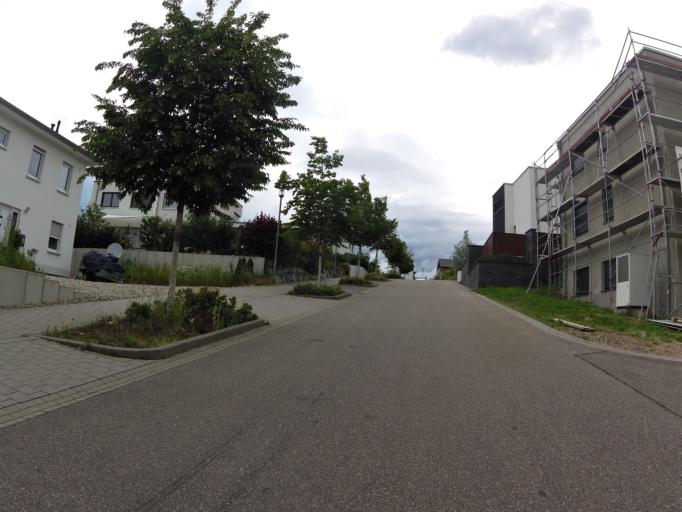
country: DE
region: Baden-Wuerttemberg
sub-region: Freiburg Region
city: Friesenheim
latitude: 48.3487
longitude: 7.8851
